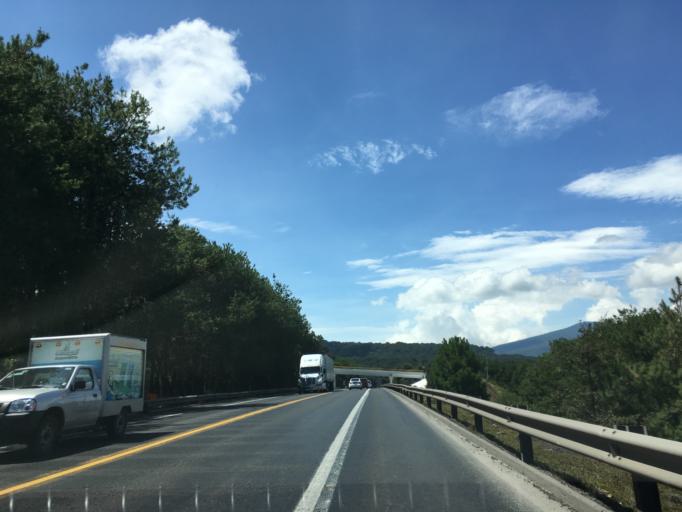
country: MX
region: Michoacan
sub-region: Patzcuaro
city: Santa Ana Chapitiro
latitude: 19.4966
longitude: -101.7005
